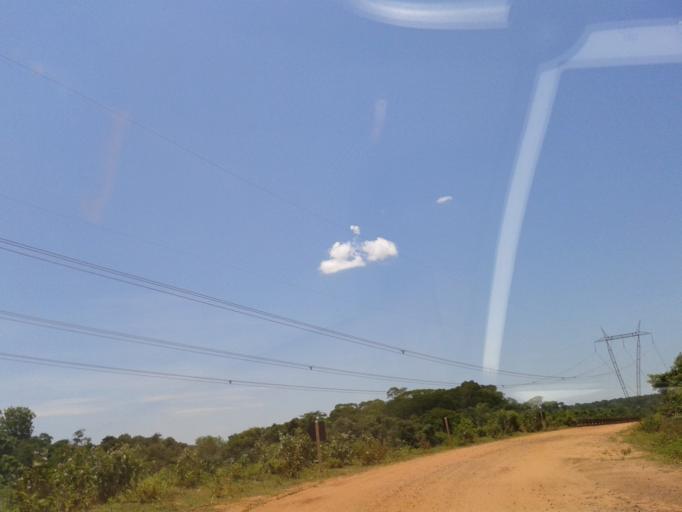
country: BR
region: Minas Gerais
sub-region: Santa Vitoria
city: Santa Vitoria
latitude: -19.2279
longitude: -50.3824
